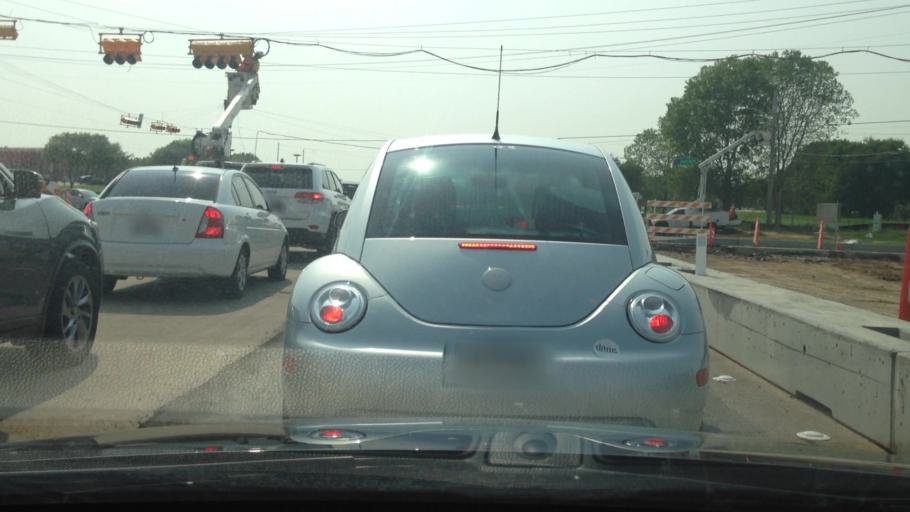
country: US
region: Texas
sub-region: Tarrant County
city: North Richland Hills
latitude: 32.8621
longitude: -97.2085
